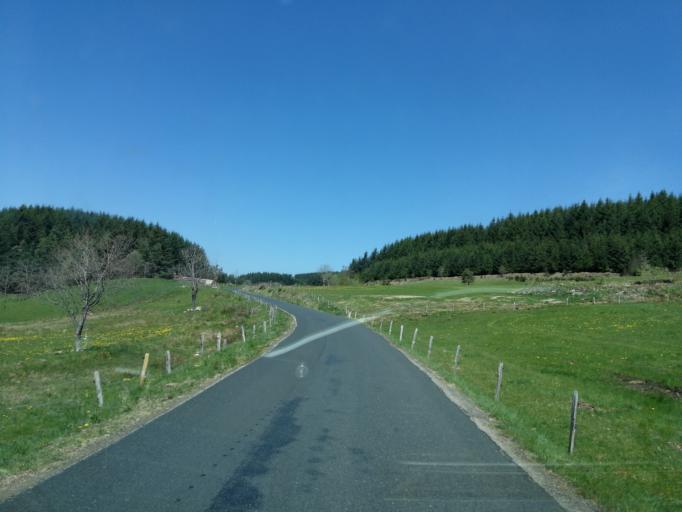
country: FR
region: Rhone-Alpes
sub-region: Departement de l'Ardeche
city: Le Cheylard
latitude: 44.9428
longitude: 4.4215
